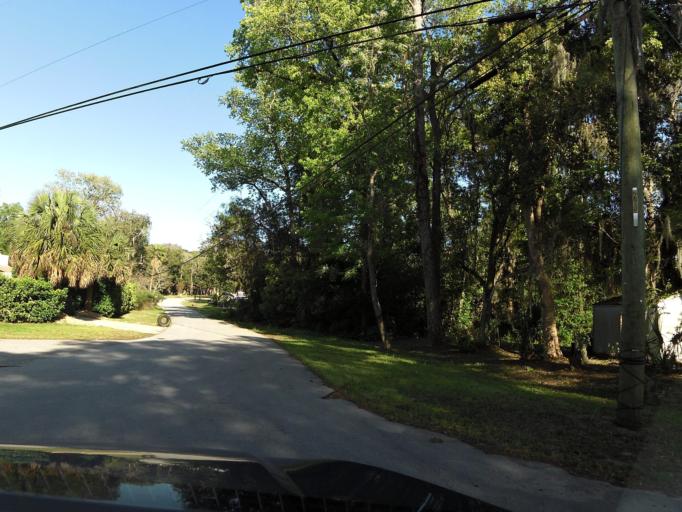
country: US
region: Florida
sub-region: Duval County
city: Jacksonville
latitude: 30.2777
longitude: -81.5743
